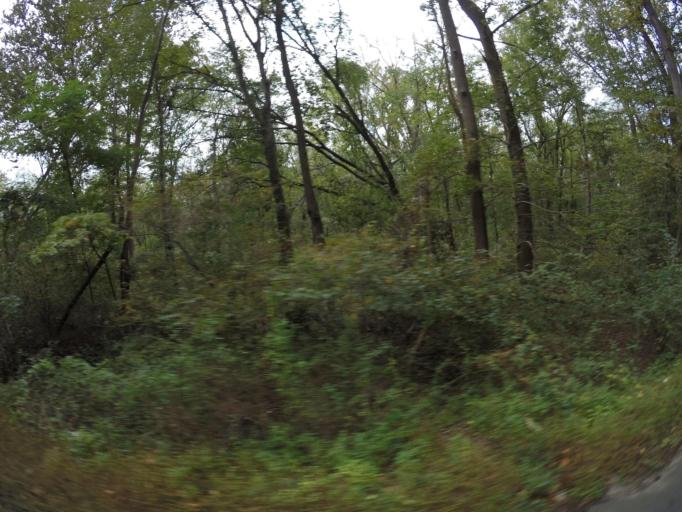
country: US
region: Delaware
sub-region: New Castle County
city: Newark
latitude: 39.7236
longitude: -75.7707
